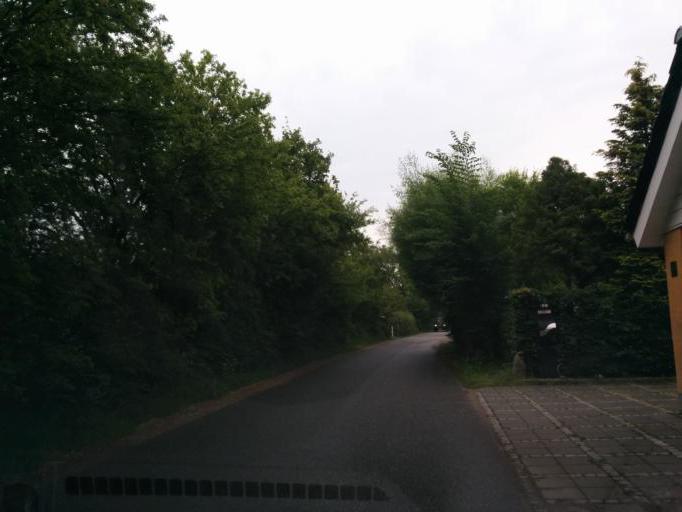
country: DK
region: Central Jutland
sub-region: Syddjurs Kommune
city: Hornslet
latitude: 56.2869
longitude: 10.3800
